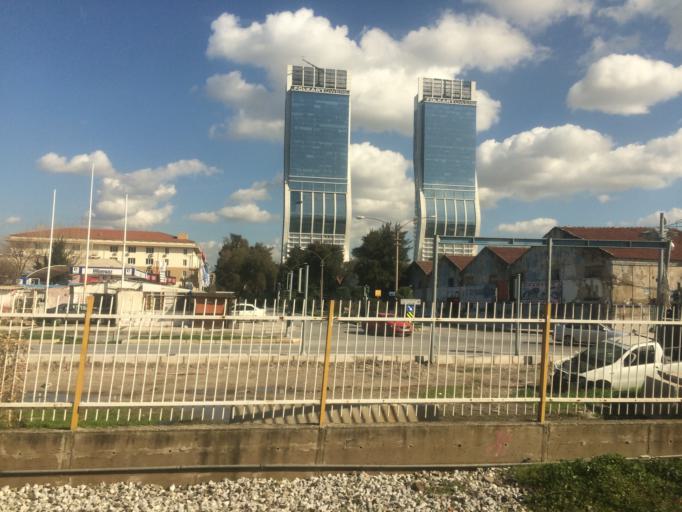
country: TR
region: Izmir
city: Izmir
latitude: 38.4533
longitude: 27.1713
